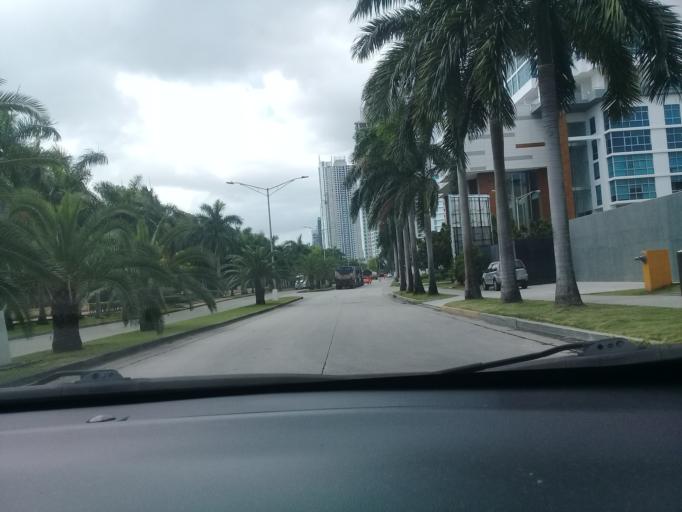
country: PA
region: Panama
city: San Miguelito
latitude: 9.0100
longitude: -79.4661
